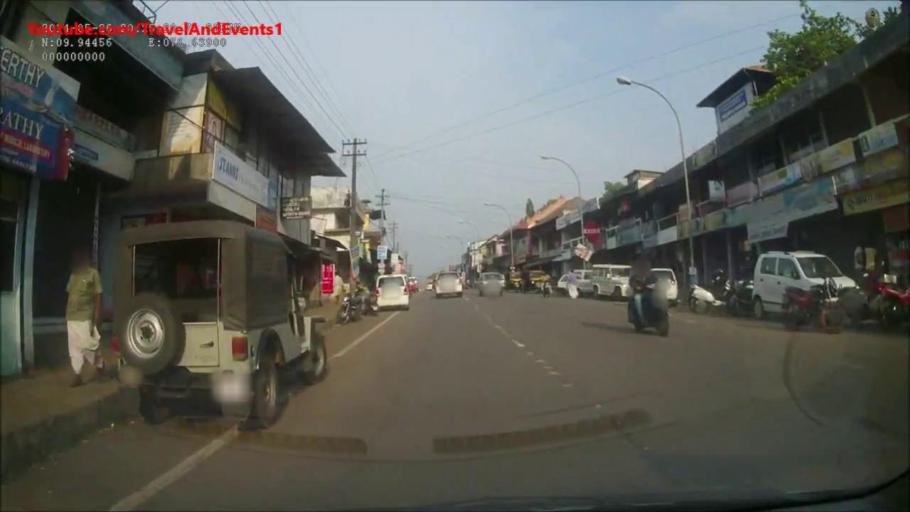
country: IN
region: Kerala
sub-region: Ernakulam
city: Muvattupula
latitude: 9.9415
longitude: 76.6447
